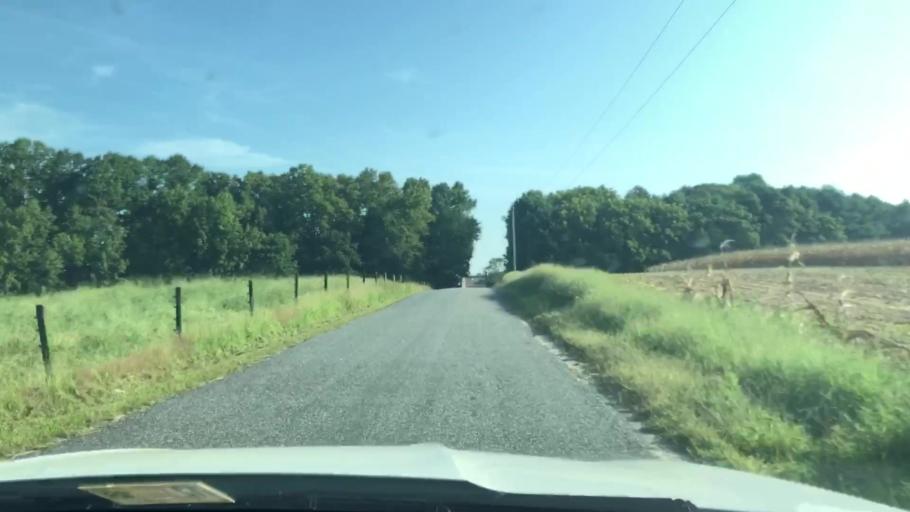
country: US
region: Virginia
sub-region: Middlesex County
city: Saluda
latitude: 37.6743
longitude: -76.6815
